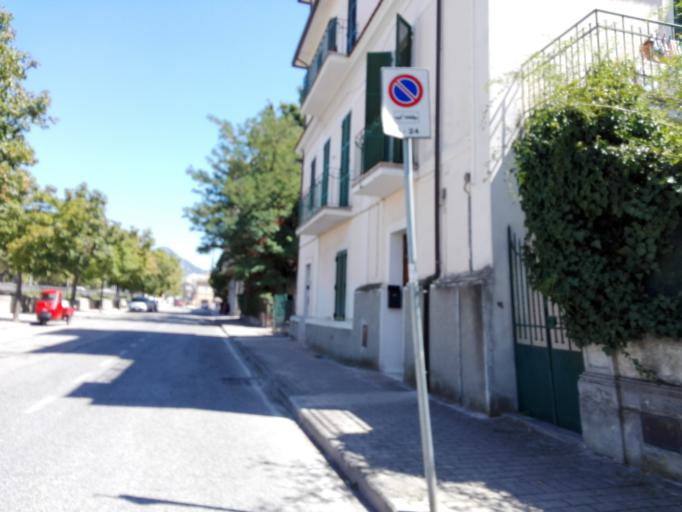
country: IT
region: Umbria
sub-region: Provincia di Perugia
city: Foligno
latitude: 42.9584
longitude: 12.7003
